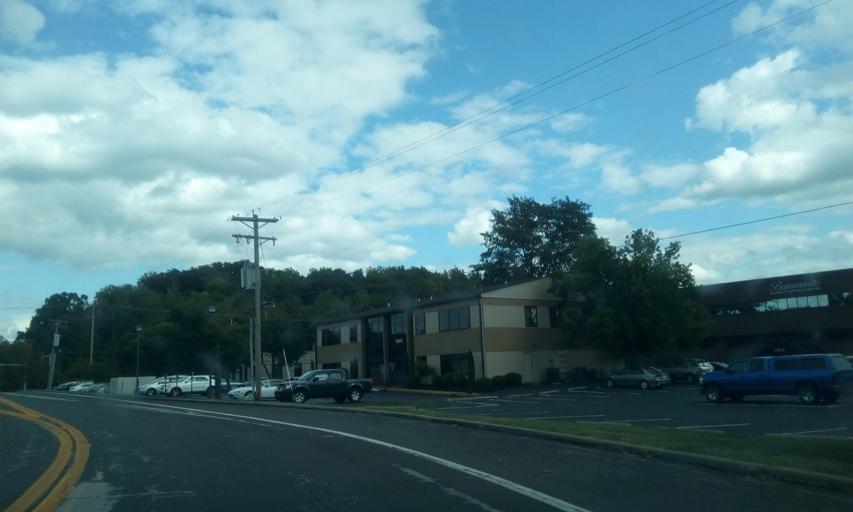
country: US
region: Missouri
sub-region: Saint Louis County
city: Town and Country
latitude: 38.5953
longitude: -90.4750
